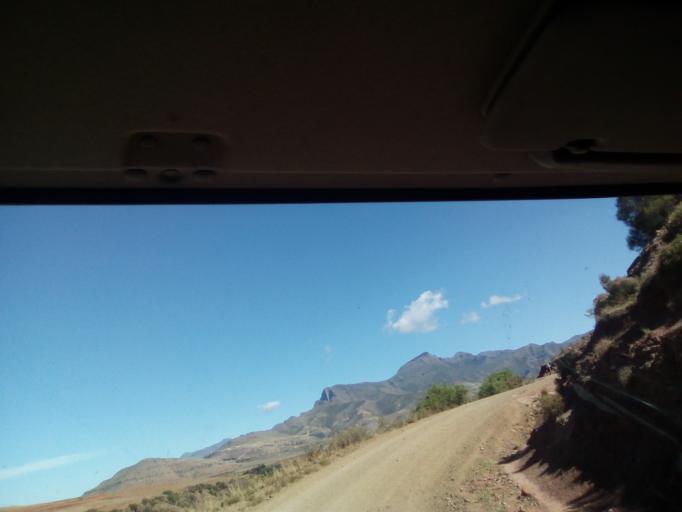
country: LS
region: Qacha's Nek
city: Qacha's Nek
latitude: -30.0577
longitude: 28.6351
